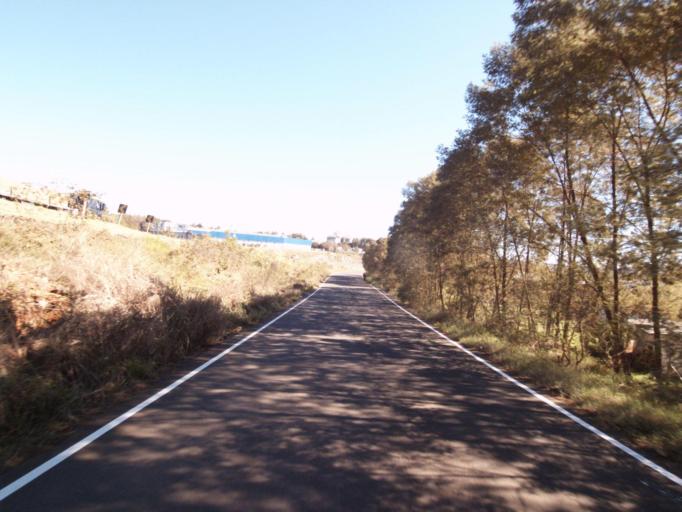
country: BR
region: Santa Catarina
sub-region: Xanxere
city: Xanxere
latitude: -26.8854
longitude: -52.3960
